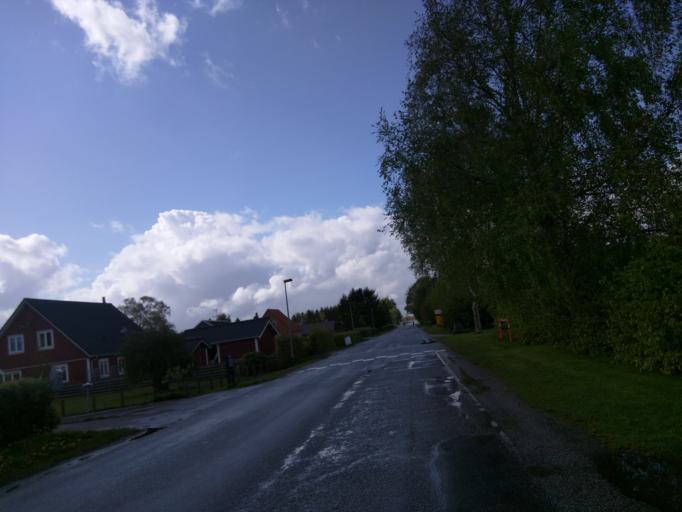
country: DK
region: Central Jutland
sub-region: Viborg Kommune
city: Viborg
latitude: 56.4144
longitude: 9.4138
